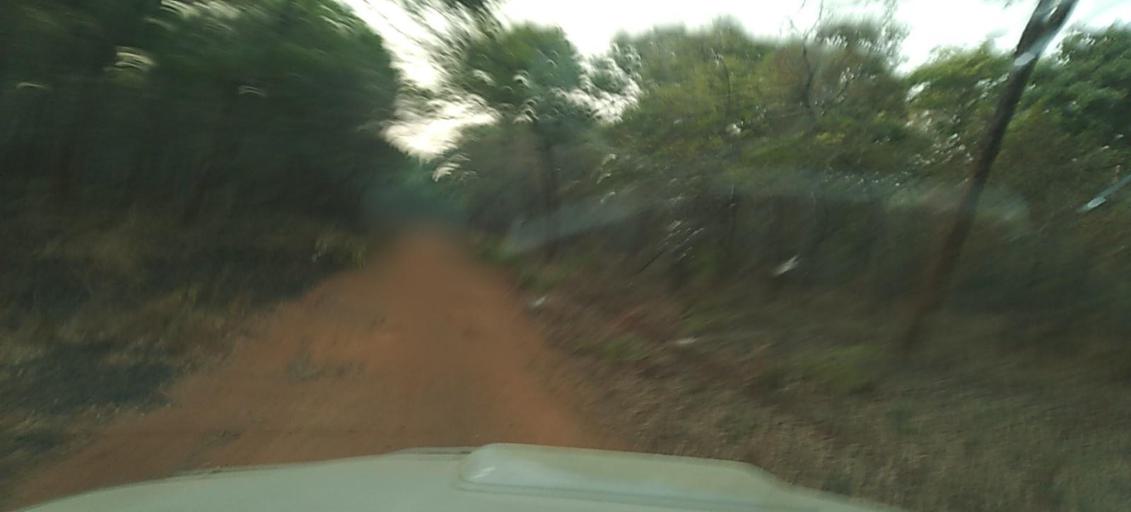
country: ZM
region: North-Western
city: Kasempa
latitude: -13.1117
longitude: 26.4060
